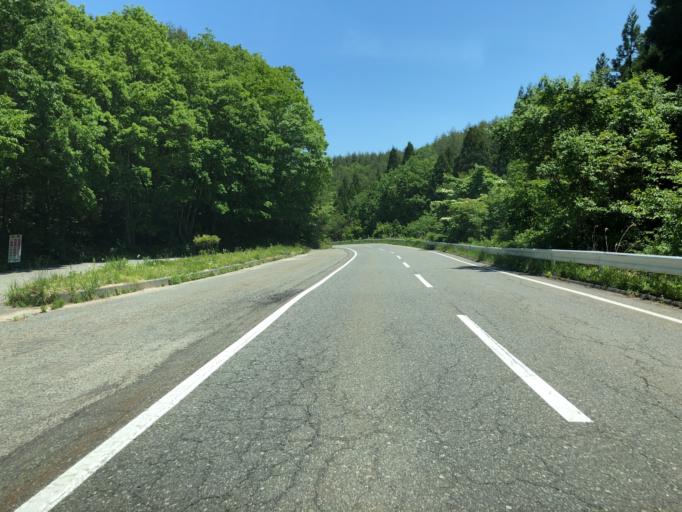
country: JP
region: Fukushima
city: Namie
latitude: 37.5206
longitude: 140.7954
